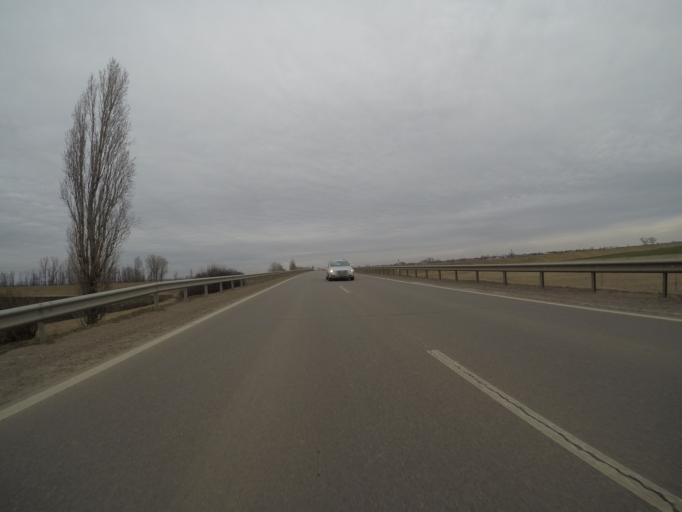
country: HU
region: Jasz-Nagykun-Szolnok
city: Jaszjakohalma
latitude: 47.5201
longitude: 19.9654
